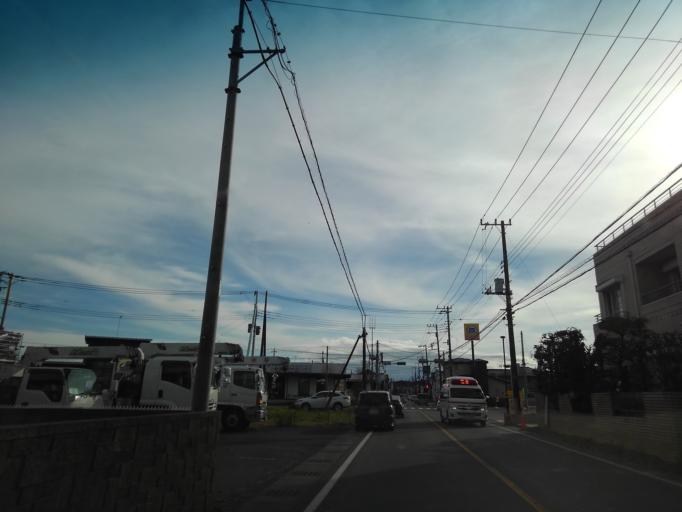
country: JP
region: Saitama
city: Morohongo
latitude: 35.9036
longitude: 139.3343
